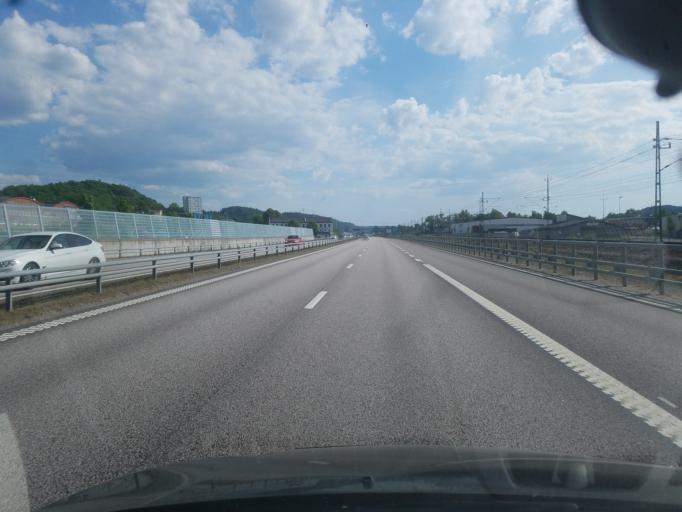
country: SE
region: Vaestra Goetaland
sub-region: Ale Kommun
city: Surte
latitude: 57.8321
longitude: 12.0133
